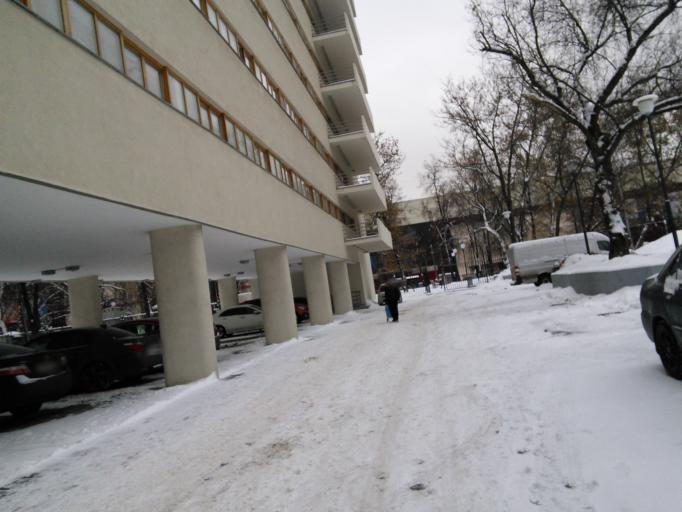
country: RU
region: Moscow
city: Novyye Cheremushki
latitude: 55.7109
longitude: 37.5954
